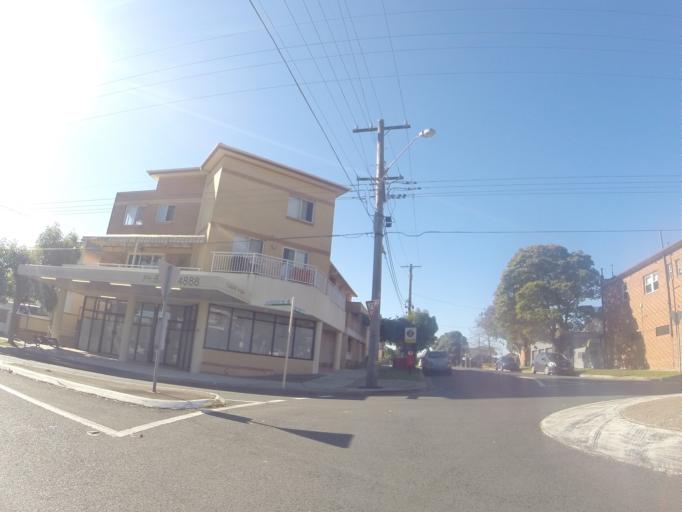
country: AU
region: New South Wales
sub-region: Hurstville
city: Earlwood
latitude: -33.9601
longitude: 151.0944
